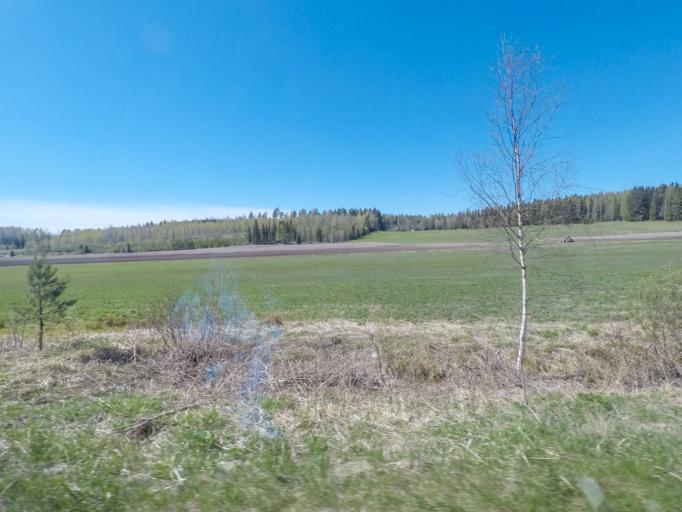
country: FI
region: Uusimaa
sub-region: Helsinki
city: Sammatti
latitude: 60.3934
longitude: 23.8139
